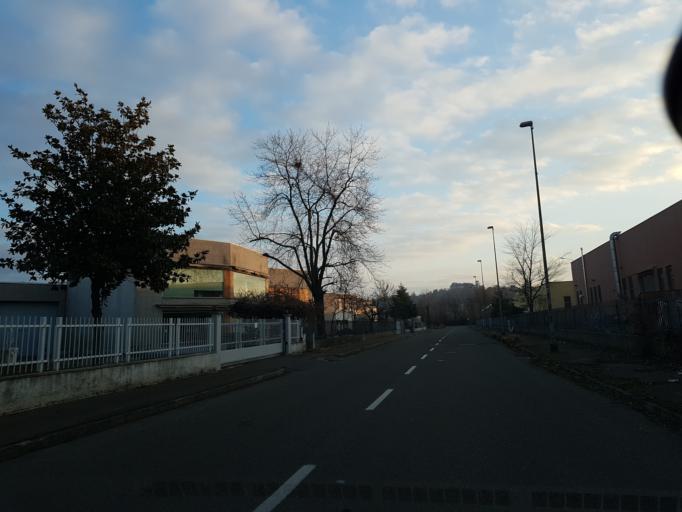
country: IT
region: Piedmont
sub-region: Provincia di Alessandria
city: Novi Ligure
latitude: 44.7536
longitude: 8.8097
